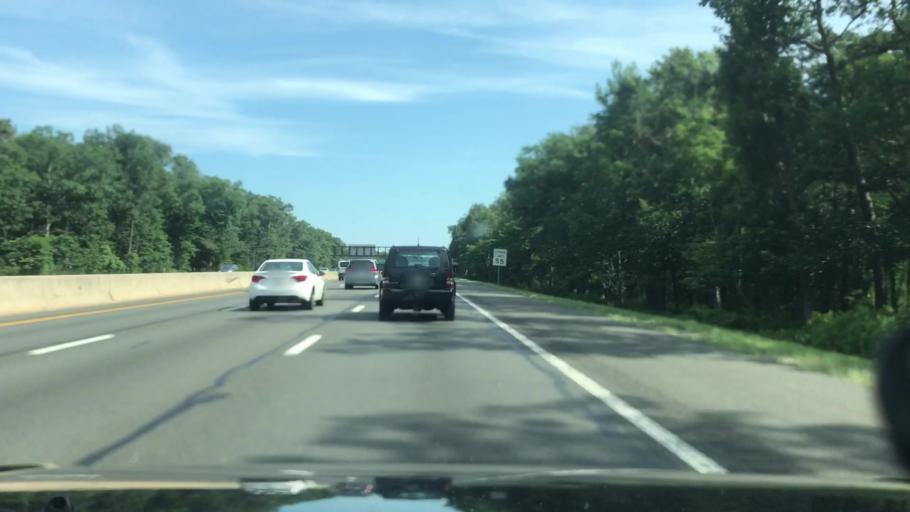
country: US
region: New Jersey
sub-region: Ocean County
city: Silver Ridge
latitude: 39.9717
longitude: -74.2096
